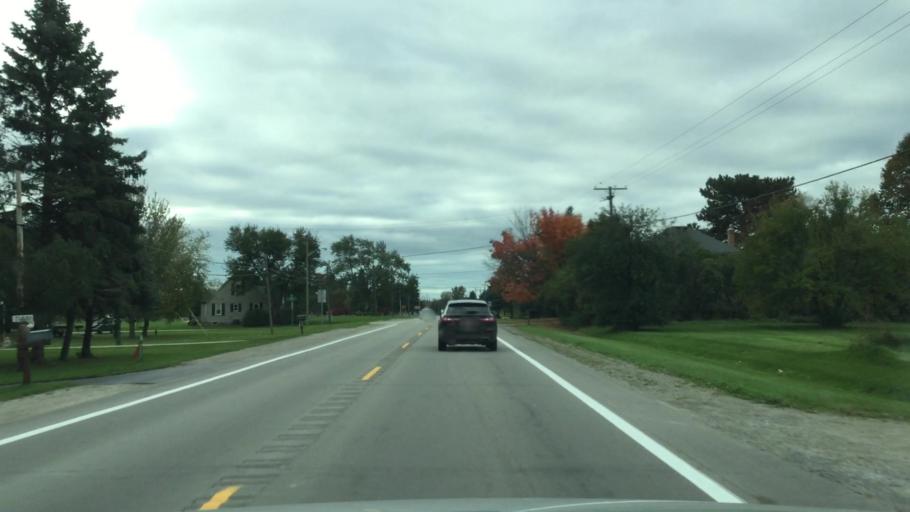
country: US
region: Michigan
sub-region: Macomb County
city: Richmond
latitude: 42.8296
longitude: -82.7617
